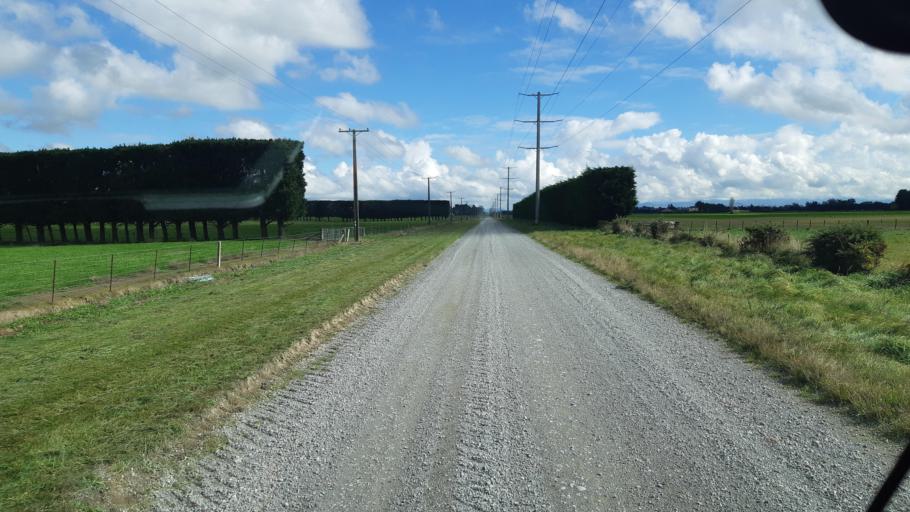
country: NZ
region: Canterbury
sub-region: Selwyn District
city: Darfield
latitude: -43.4728
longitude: 172.2532
